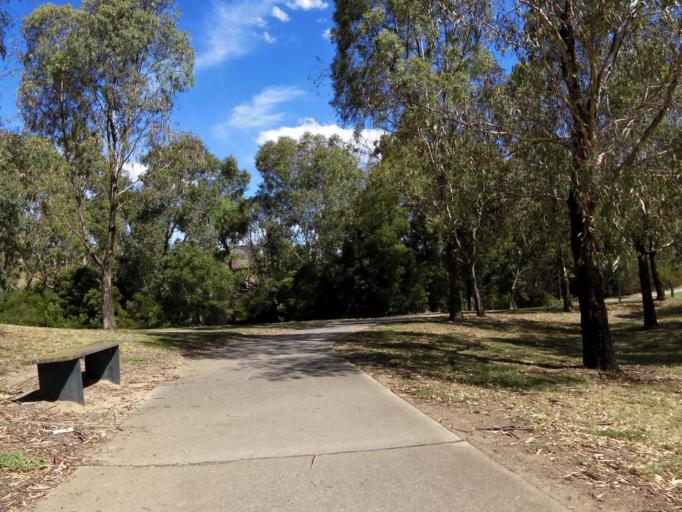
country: AU
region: Victoria
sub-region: Hume
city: Westmeadows
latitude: -37.6743
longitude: 144.8919
